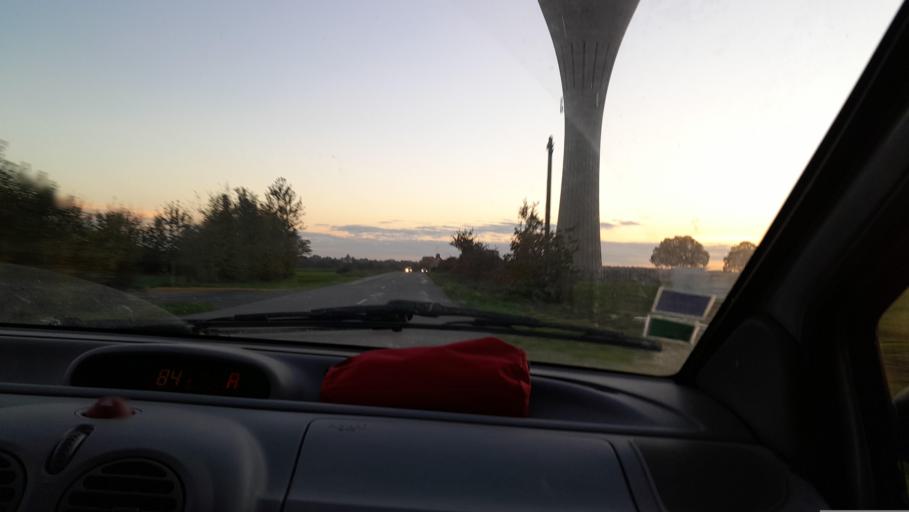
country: FR
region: Pays de la Loire
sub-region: Departement de la Mayenne
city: Ballots
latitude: 47.9114
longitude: -1.1008
